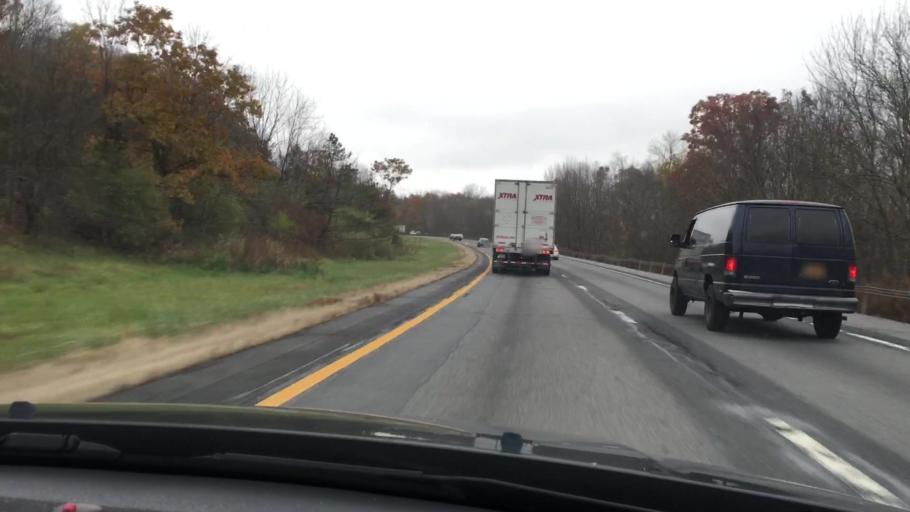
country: US
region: New York
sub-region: Putnam County
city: Lake Carmel
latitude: 41.4985
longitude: -73.6691
